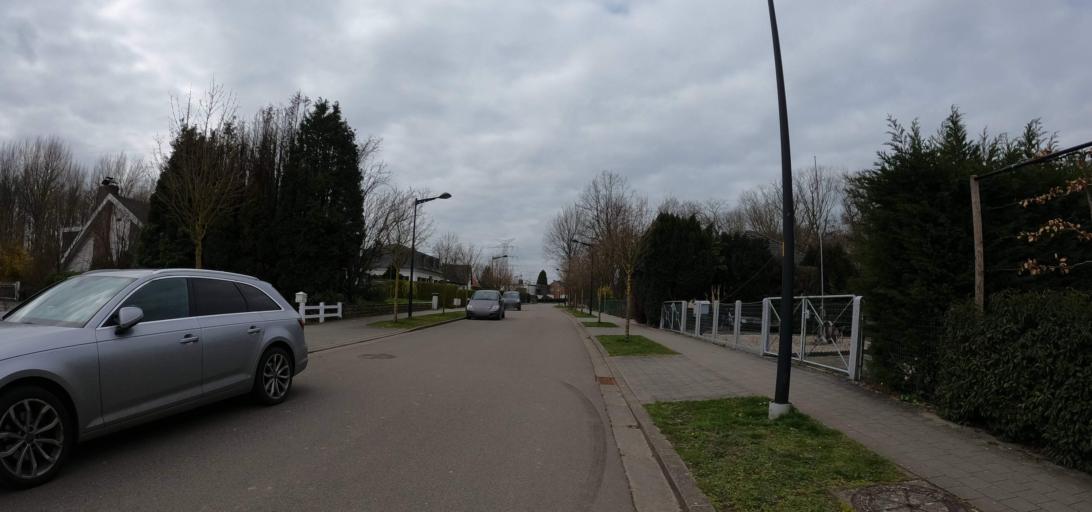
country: BE
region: Flanders
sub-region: Provincie Oost-Vlaanderen
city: Kruibeke
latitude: 51.1379
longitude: 4.3010
